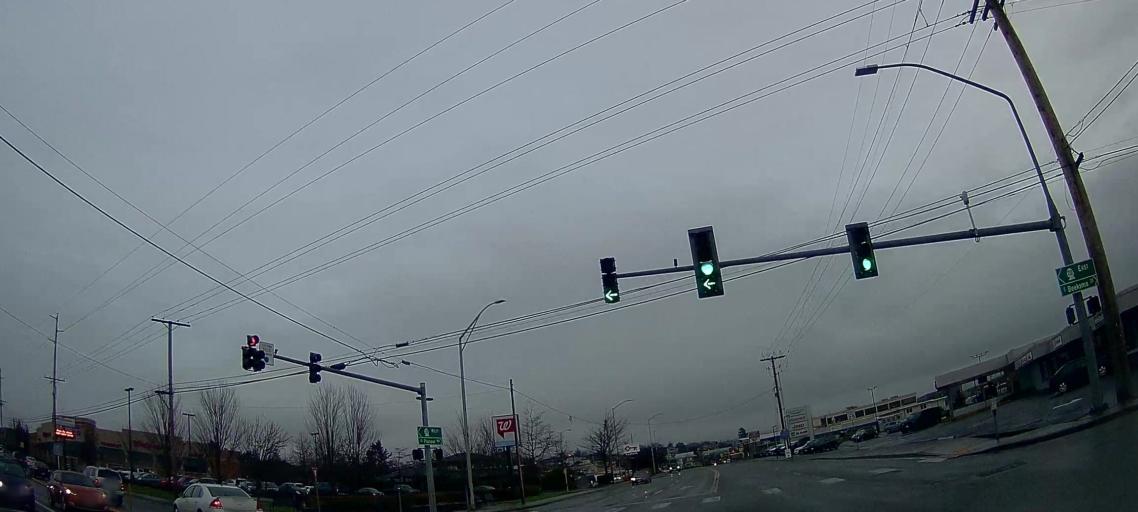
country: US
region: Washington
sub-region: Island County
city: Oak Harbor
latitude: 48.2869
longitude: -122.6578
